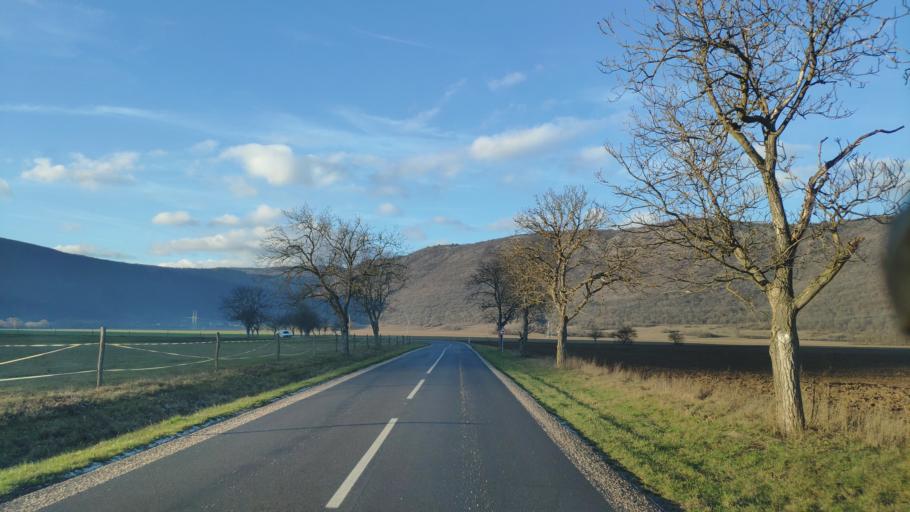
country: SK
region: Kosicky
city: Medzev
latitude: 48.6137
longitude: 20.8823
